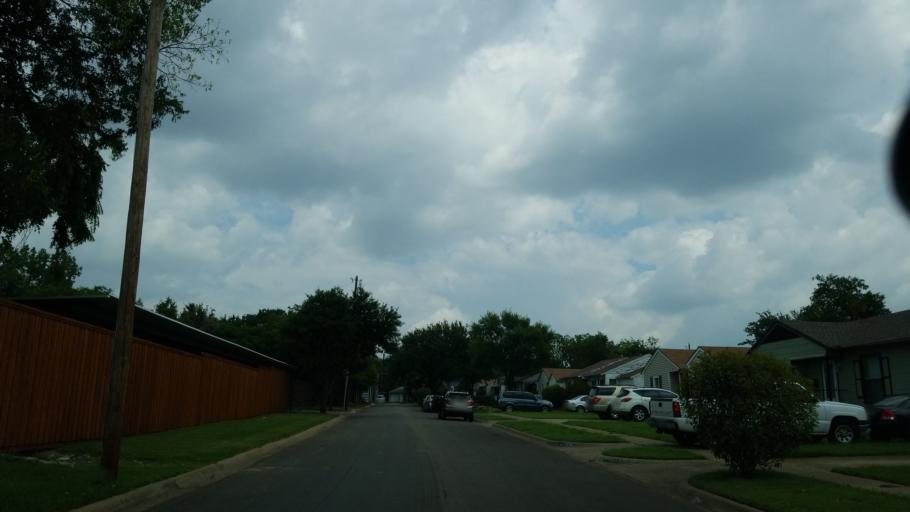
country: US
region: Texas
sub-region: Dallas County
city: University Park
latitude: 32.8502
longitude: -96.8319
